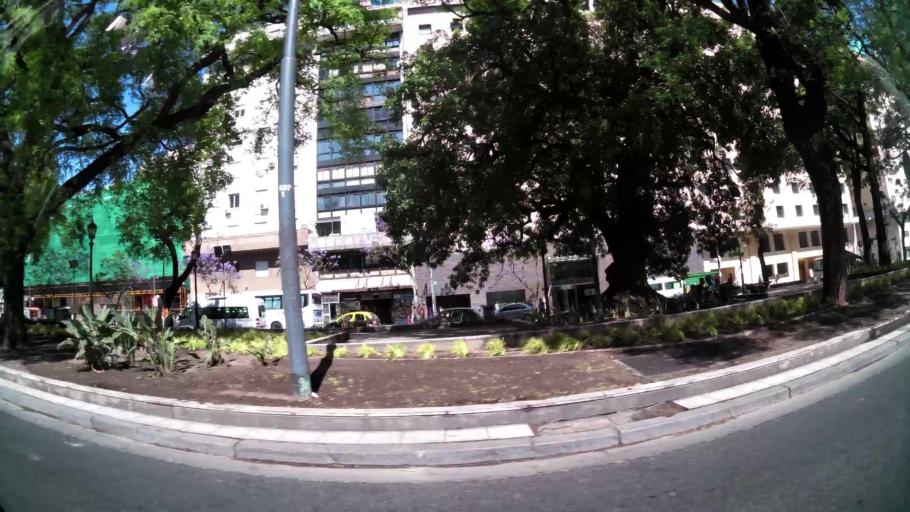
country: AR
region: Buenos Aires F.D.
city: Buenos Aires
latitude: -34.6068
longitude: -58.3818
